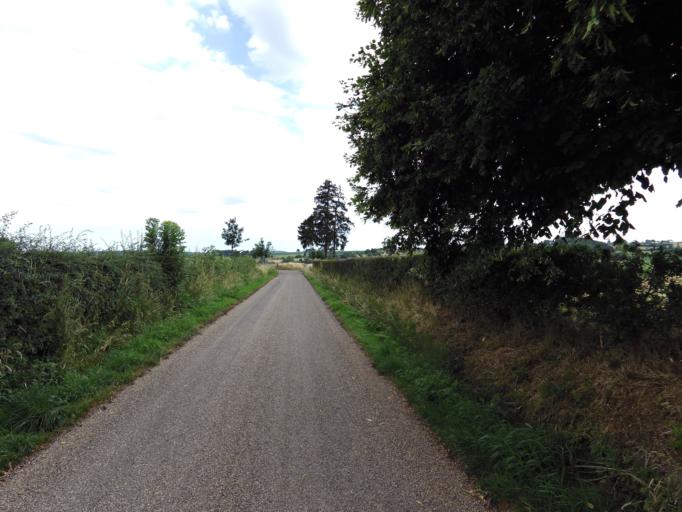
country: BE
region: Wallonia
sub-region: Province de Liege
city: Plombieres
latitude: 50.7909
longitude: 5.9393
